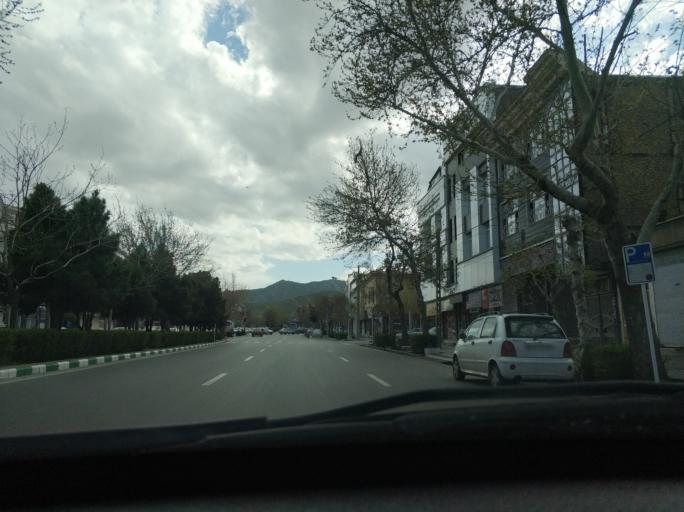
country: IR
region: Razavi Khorasan
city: Mashhad
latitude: 36.2682
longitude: 59.5877
